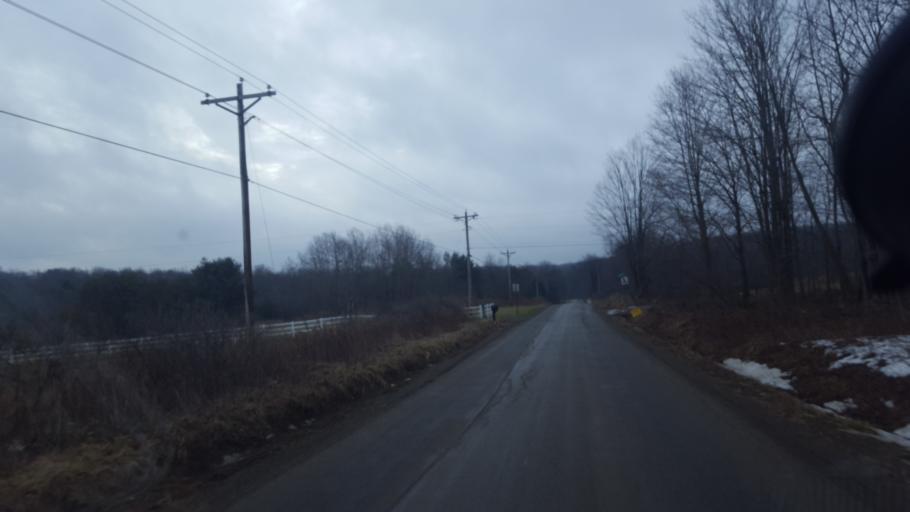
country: US
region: New York
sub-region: Allegany County
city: Andover
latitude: 41.9763
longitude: -77.7397
